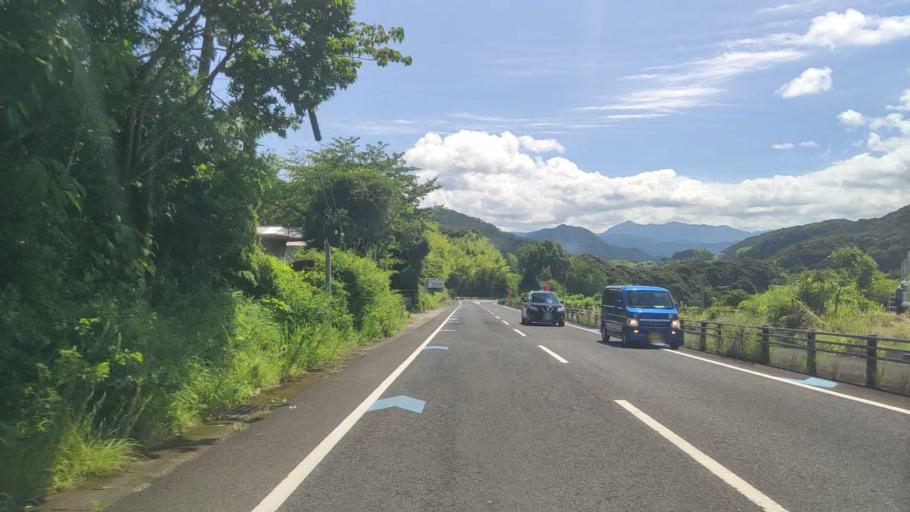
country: JP
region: Wakayama
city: Shingu
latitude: 33.7437
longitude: 136.0087
